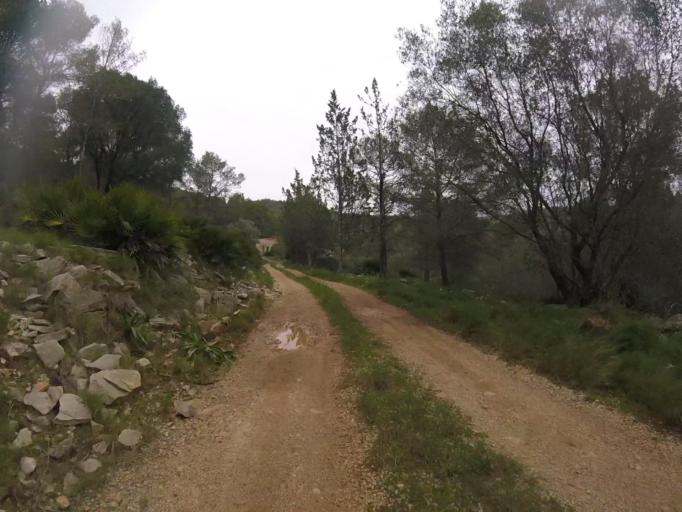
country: ES
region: Valencia
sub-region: Provincia de Castello
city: Santa Magdalena de Pulpis
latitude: 40.3192
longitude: 0.2809
